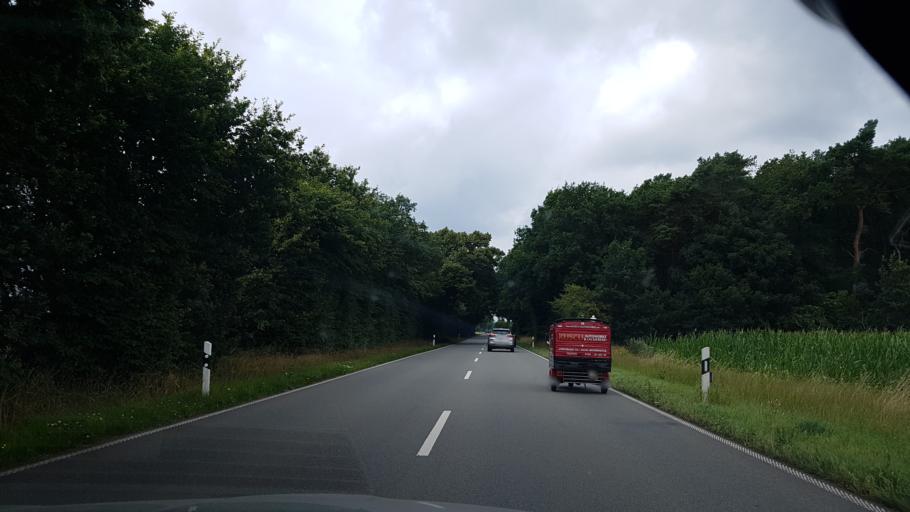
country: DE
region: Schleswig-Holstein
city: Gross Kummerfeld
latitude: 54.0277
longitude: 10.0873
